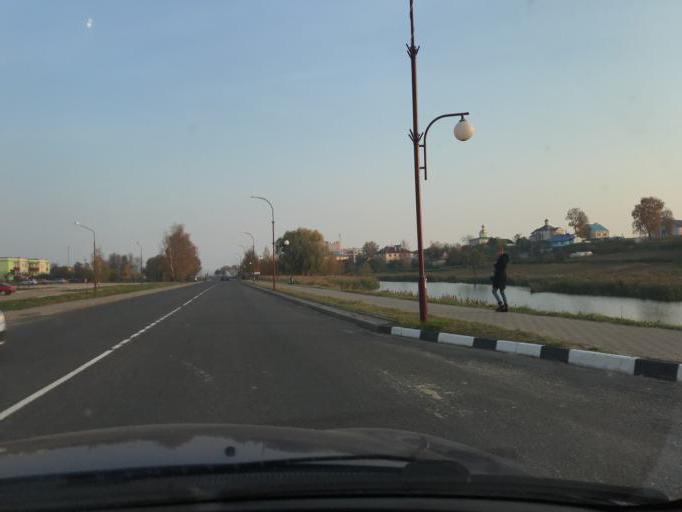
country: BY
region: Grodnenskaya
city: Karelichy
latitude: 53.5749
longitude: 26.1345
